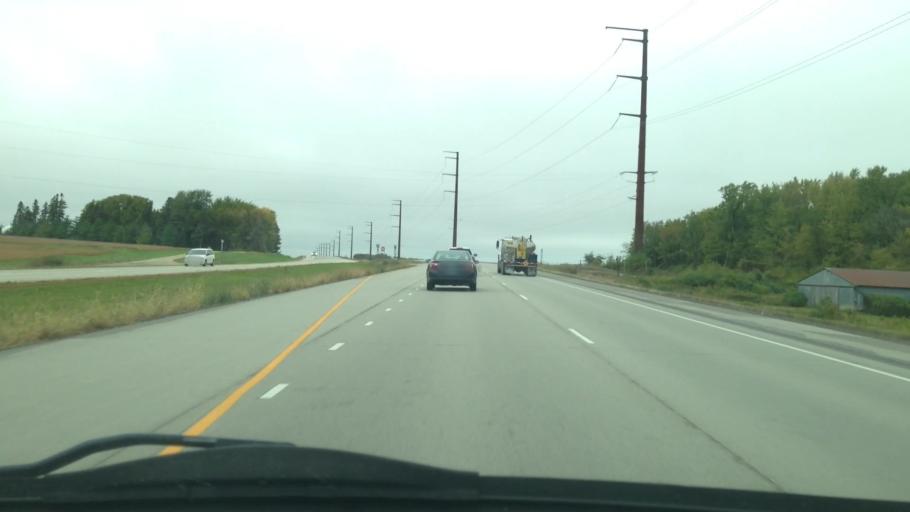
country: US
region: Minnesota
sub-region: Goodhue County
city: Wanamingo
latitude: 44.3710
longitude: -92.8048
